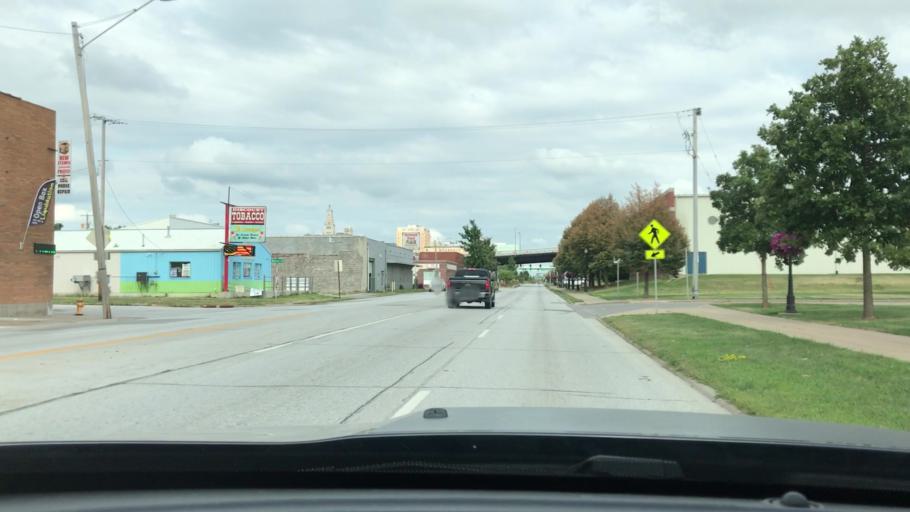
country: US
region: Iowa
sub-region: Scott County
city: Davenport
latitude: 41.5201
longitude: -90.5864
